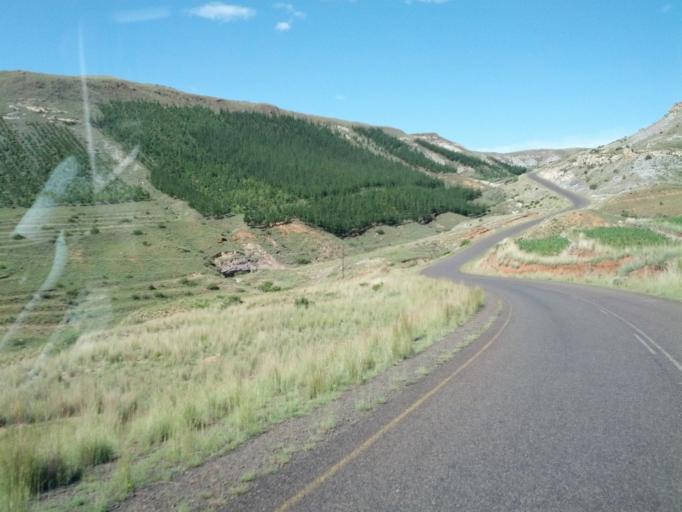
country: LS
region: Qacha's Nek
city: Qacha's Nek
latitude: -30.0732
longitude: 28.5644
